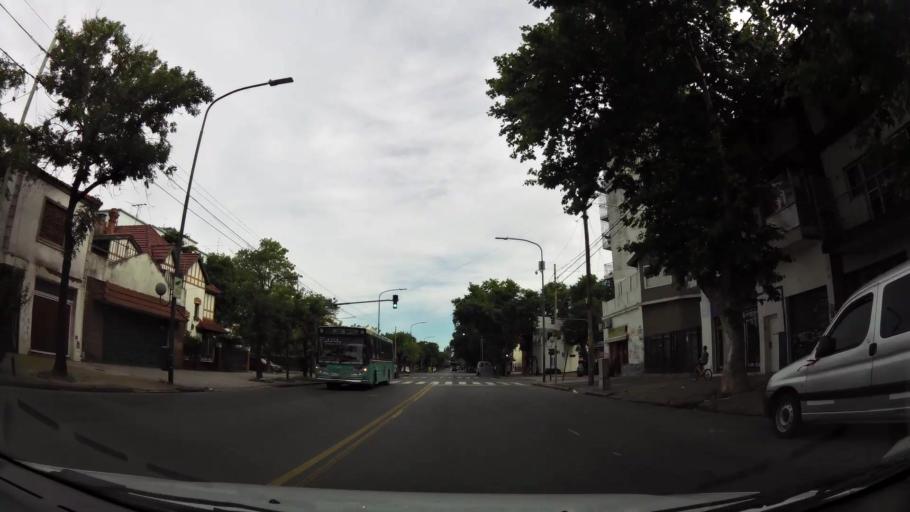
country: AR
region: Buenos Aires F.D.
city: Villa Santa Rita
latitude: -34.6425
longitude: -58.4855
